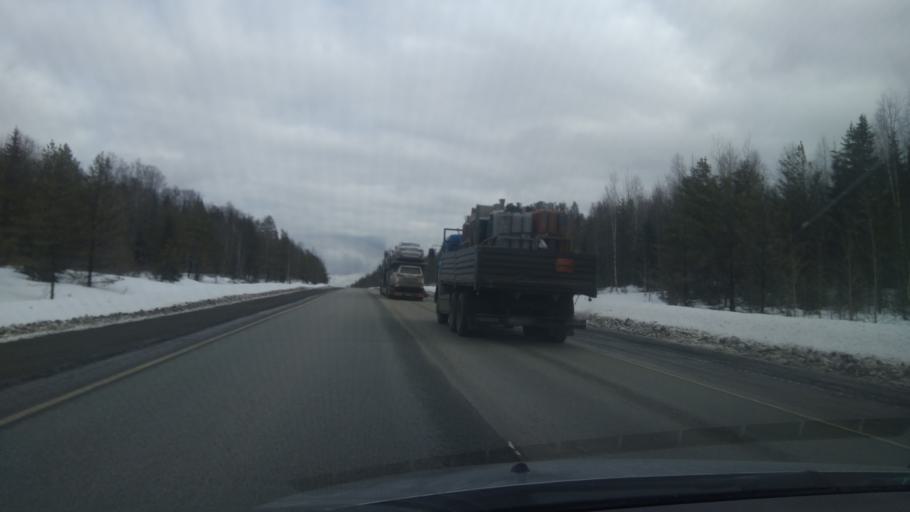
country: RU
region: Sverdlovsk
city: Nizhniye Sergi
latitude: 56.8253
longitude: 59.2398
